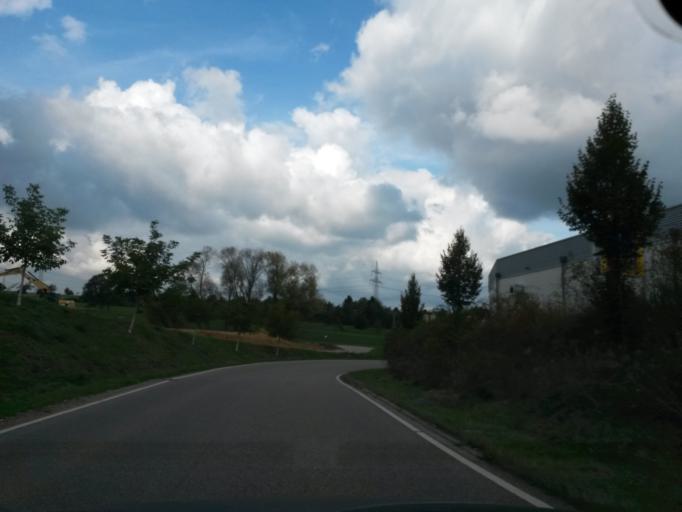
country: DE
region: Baden-Wuerttemberg
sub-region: Karlsruhe Region
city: Ettlingen
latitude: 48.9207
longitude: 8.4985
